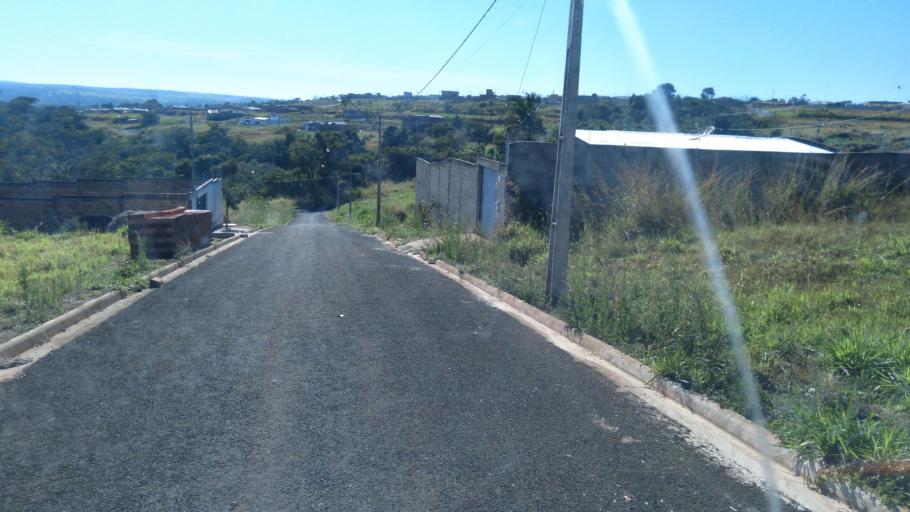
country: BR
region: Goias
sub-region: Mineiros
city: Mineiros
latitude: -17.5462
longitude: -52.5620
